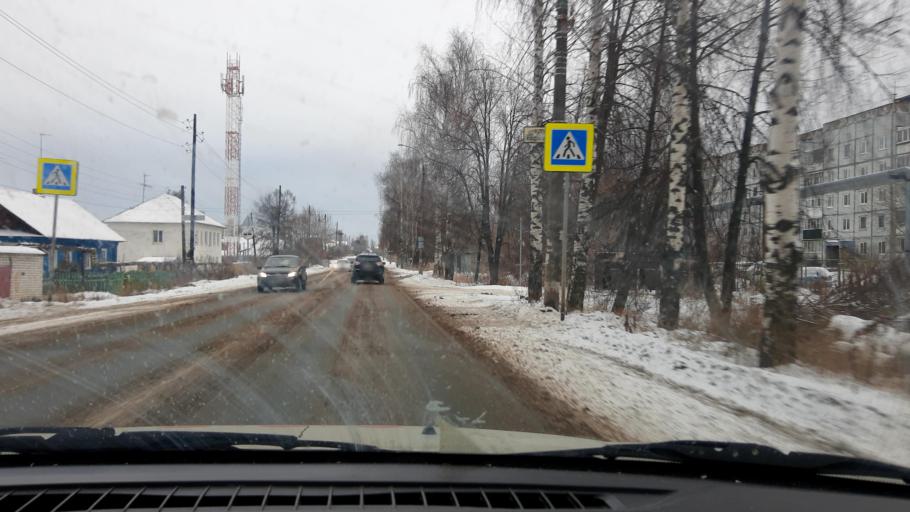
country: RU
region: Nizjnij Novgorod
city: Gorodets
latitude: 56.6496
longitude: 43.4892
